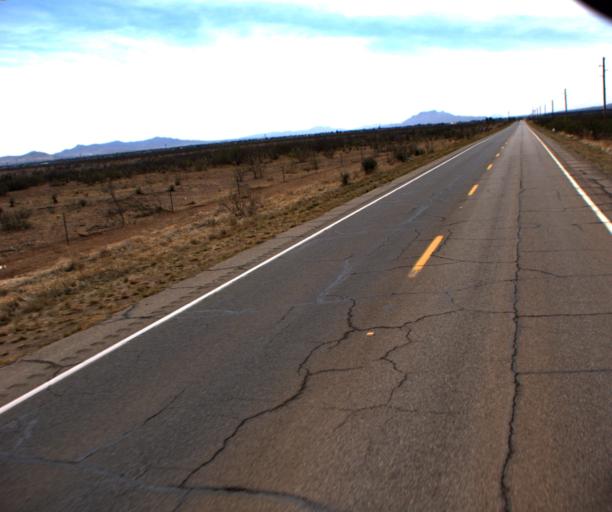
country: US
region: Arizona
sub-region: Cochise County
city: Pirtleville
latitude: 31.3862
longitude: -109.5793
